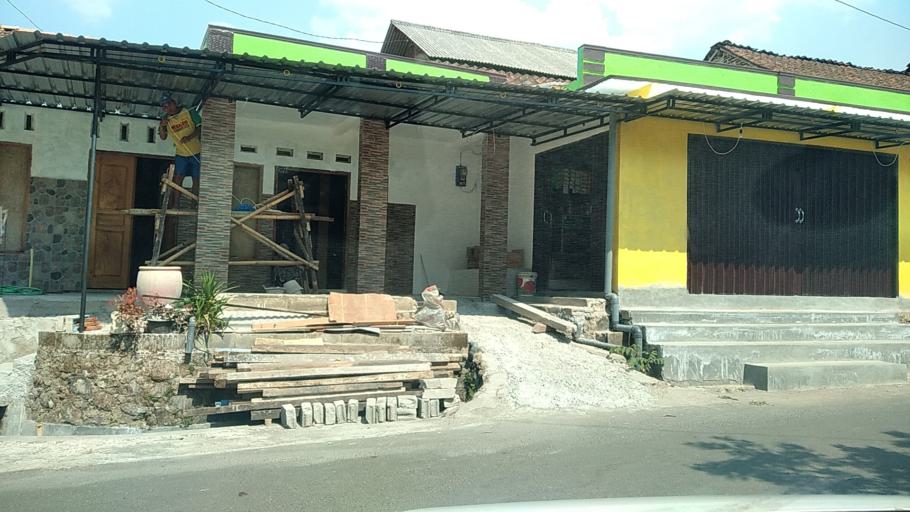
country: ID
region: Central Java
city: Ungaran
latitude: -7.0928
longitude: 110.3357
